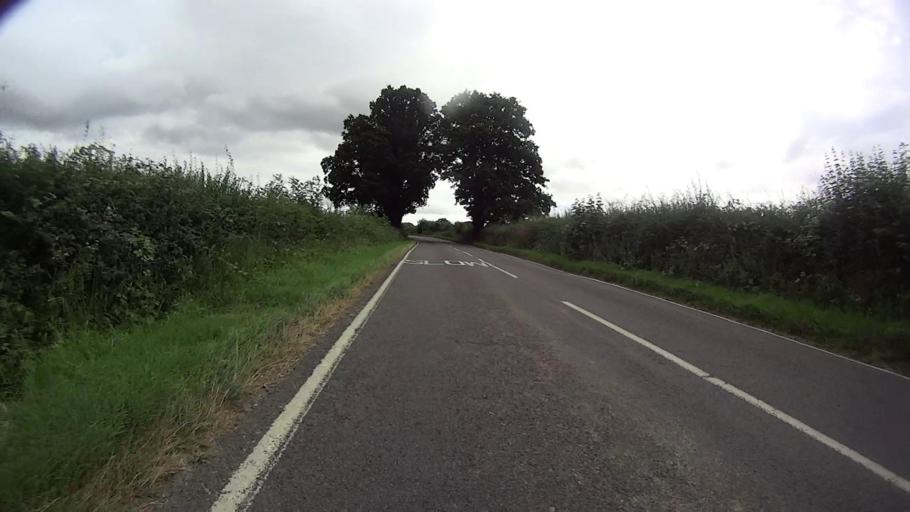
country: GB
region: England
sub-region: Surrey
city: Reigate
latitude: 51.1812
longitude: -0.2309
